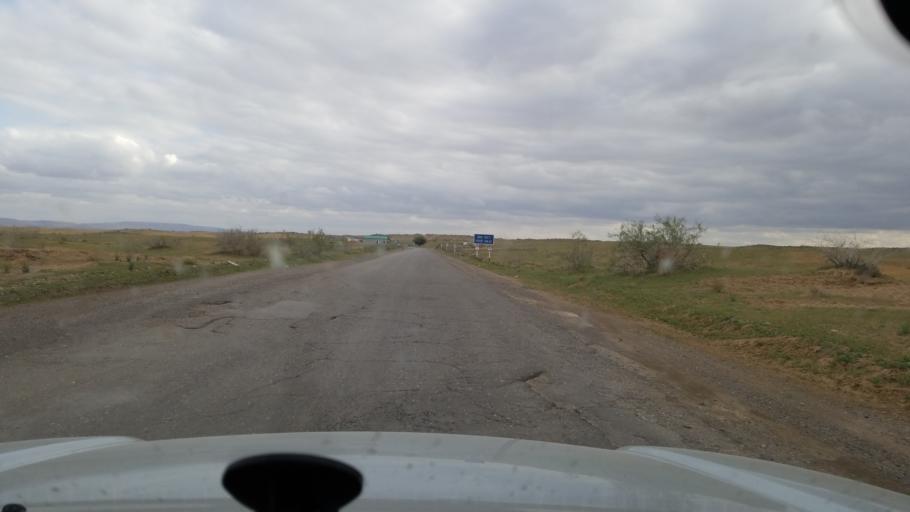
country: TM
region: Mary
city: Serhetabat
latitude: 35.9927
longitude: 62.6271
